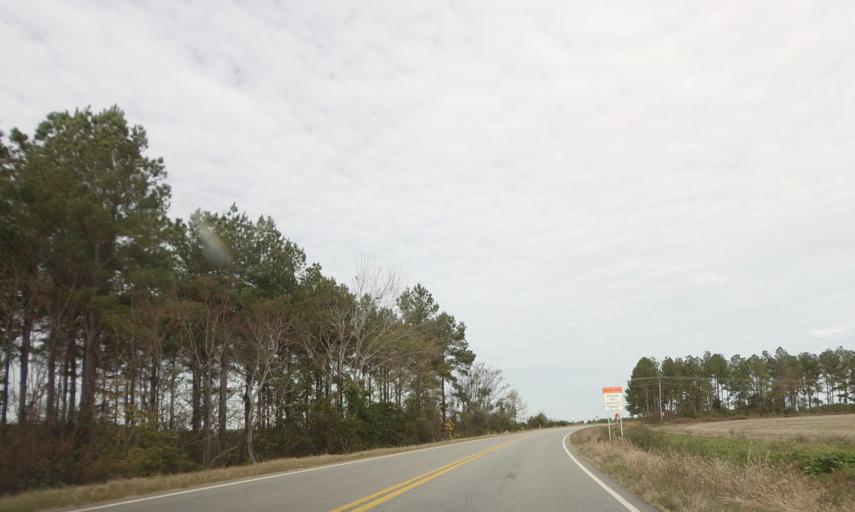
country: US
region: Georgia
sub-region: Dodge County
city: Chester
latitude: 32.5174
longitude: -83.0946
